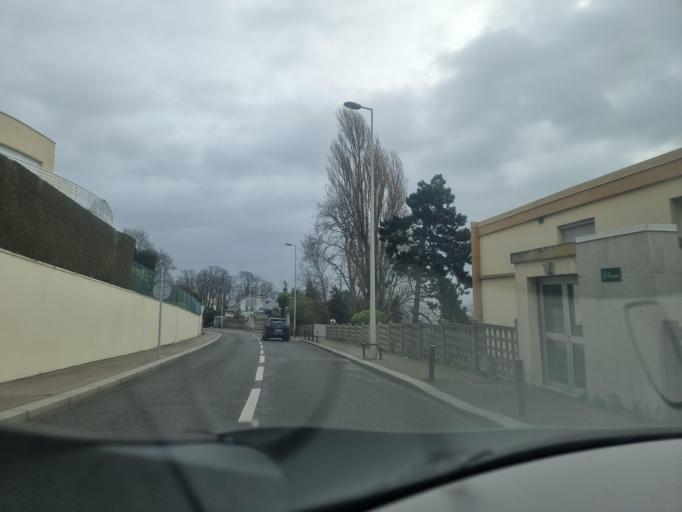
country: FR
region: Haute-Normandie
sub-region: Departement de la Seine-Maritime
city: Le Havre
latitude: 49.4993
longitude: 0.0987
